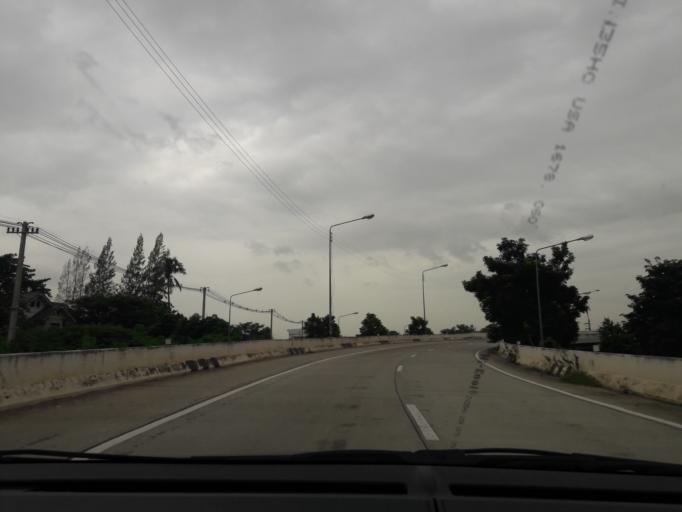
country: TH
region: Sara Buri
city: Saraburi
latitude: 14.5392
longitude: 100.9547
